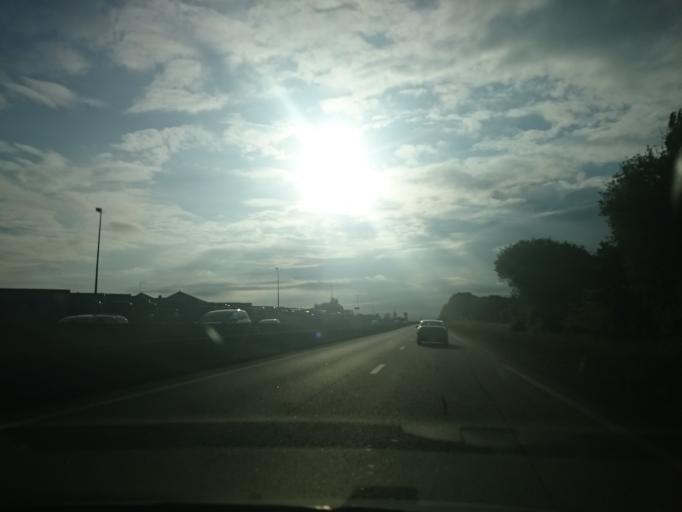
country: FR
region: Brittany
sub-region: Departement du Morbihan
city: Vannes
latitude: 47.6628
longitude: -2.7138
